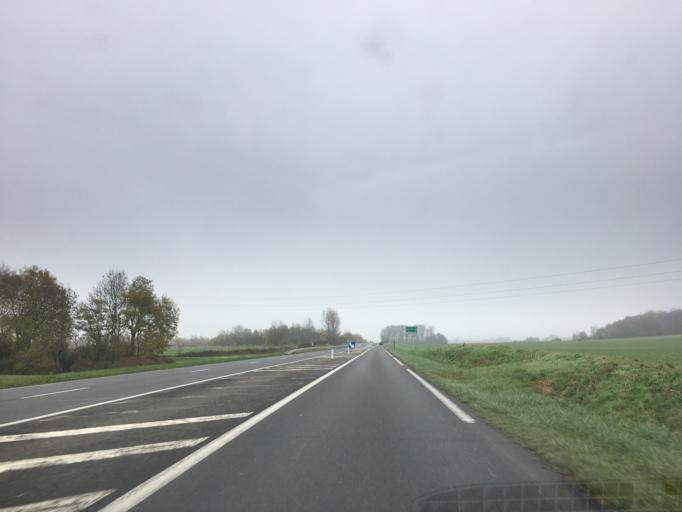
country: FR
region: Ile-de-France
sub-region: Departement de Seine-et-Marne
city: La Grande-Paroisse
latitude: 48.3613
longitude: 2.8828
